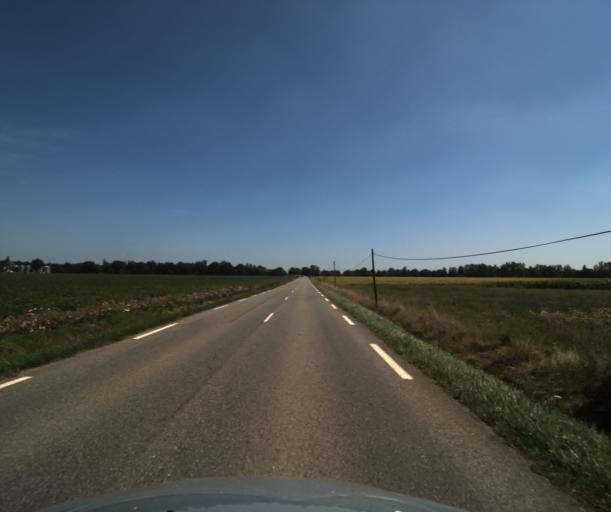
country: FR
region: Midi-Pyrenees
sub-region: Departement de la Haute-Garonne
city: Fonsorbes
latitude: 43.5071
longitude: 1.2373
